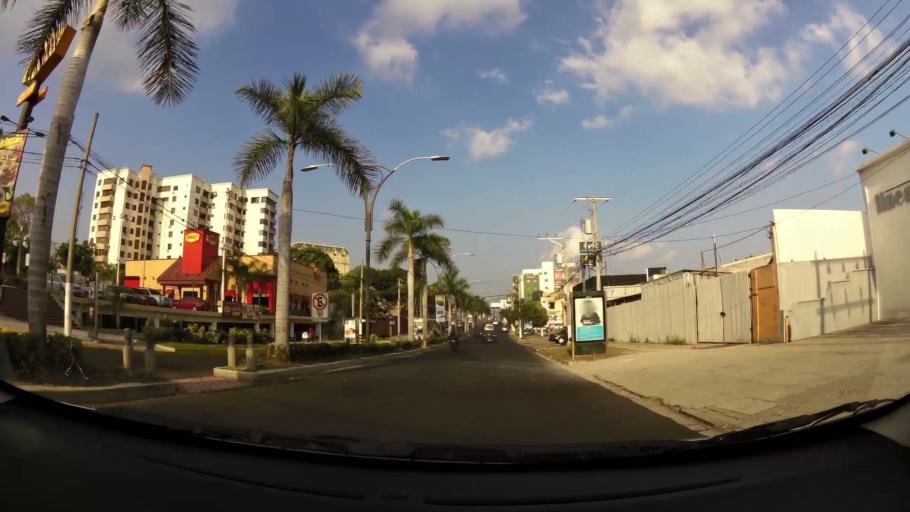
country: SV
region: La Libertad
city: Antiguo Cuscatlan
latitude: 13.6900
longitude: -89.2395
